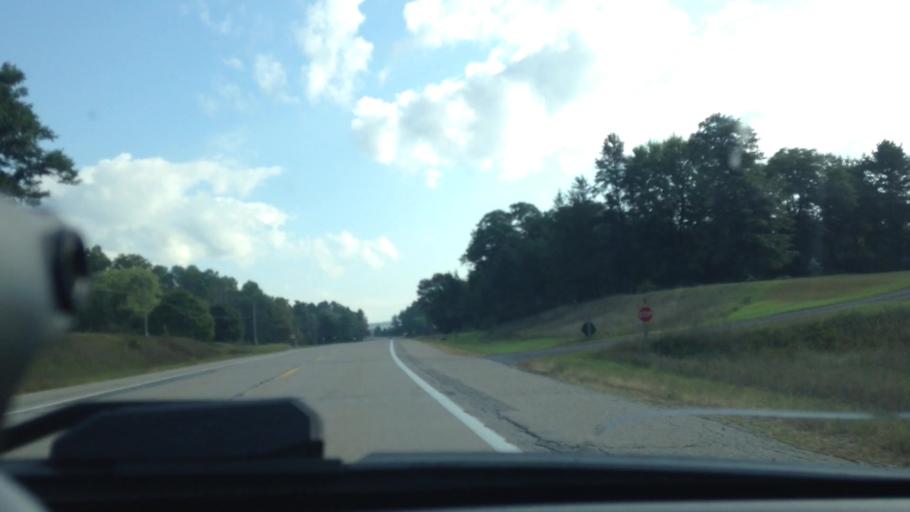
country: US
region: Michigan
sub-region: Dickinson County
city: Norway
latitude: 45.7656
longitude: -87.9170
